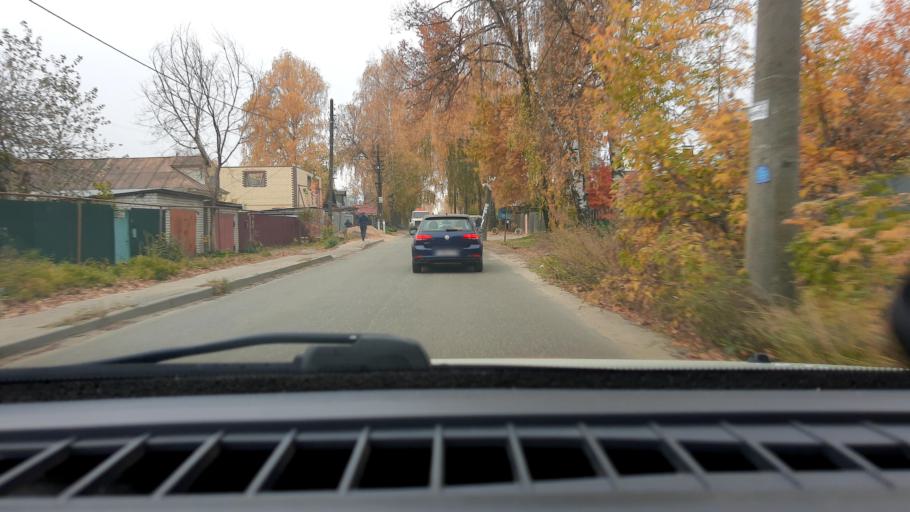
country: RU
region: Nizjnij Novgorod
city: Gorbatovka
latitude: 56.3382
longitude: 43.8304
